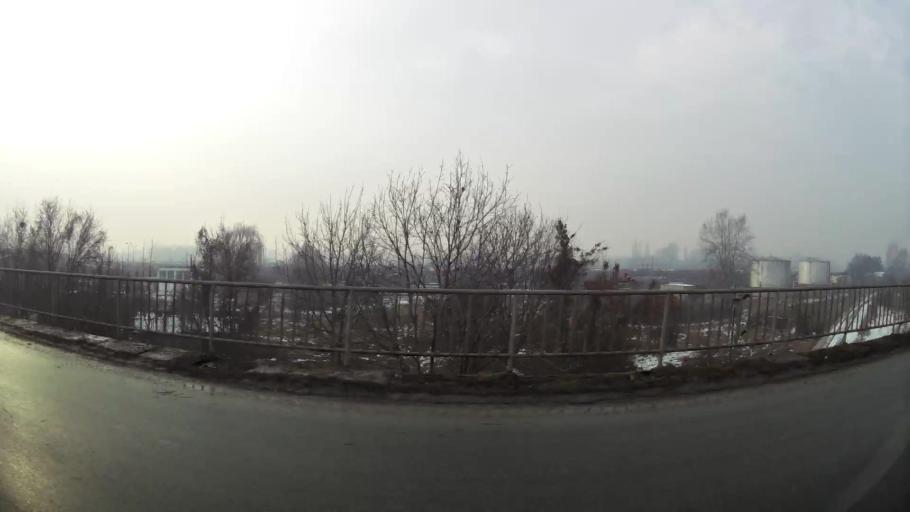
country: MK
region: Ilinden
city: Jurumleri
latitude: 41.9759
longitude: 21.5353
